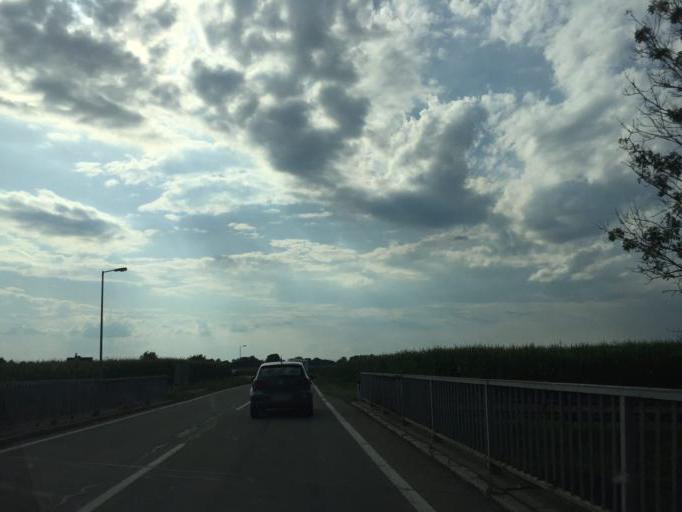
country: AT
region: Styria
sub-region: Politischer Bezirk Suedoststeiermark
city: Deutsch Goritz
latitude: 46.7301
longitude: 15.8487
